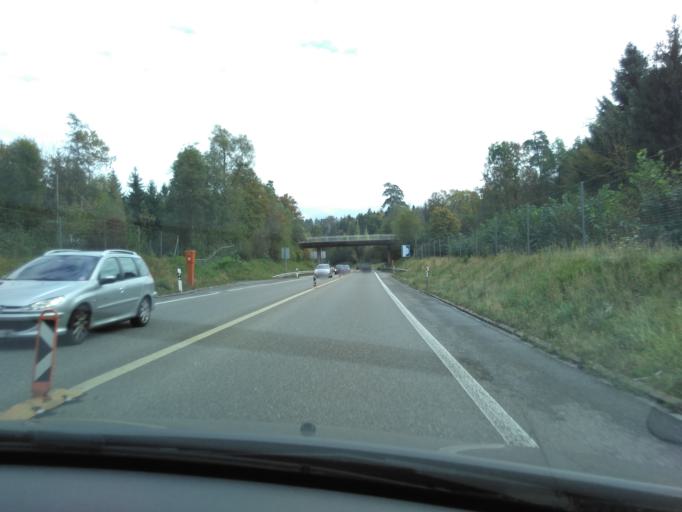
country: CH
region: Zurich
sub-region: Bezirk Hinwil
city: Rueti / Dorfzentrum, Suedl. Teil
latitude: 47.2454
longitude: 8.8521
